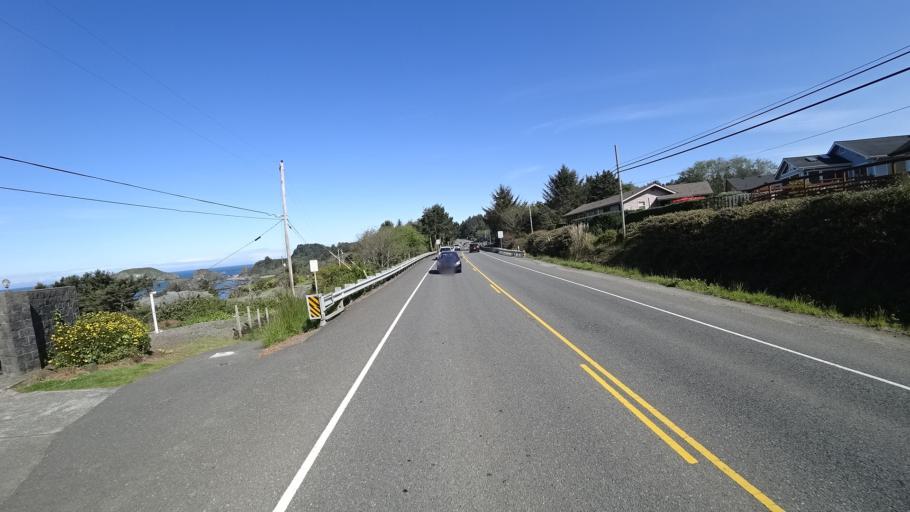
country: US
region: Oregon
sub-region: Curry County
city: Brookings
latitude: 42.0615
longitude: -124.3012
